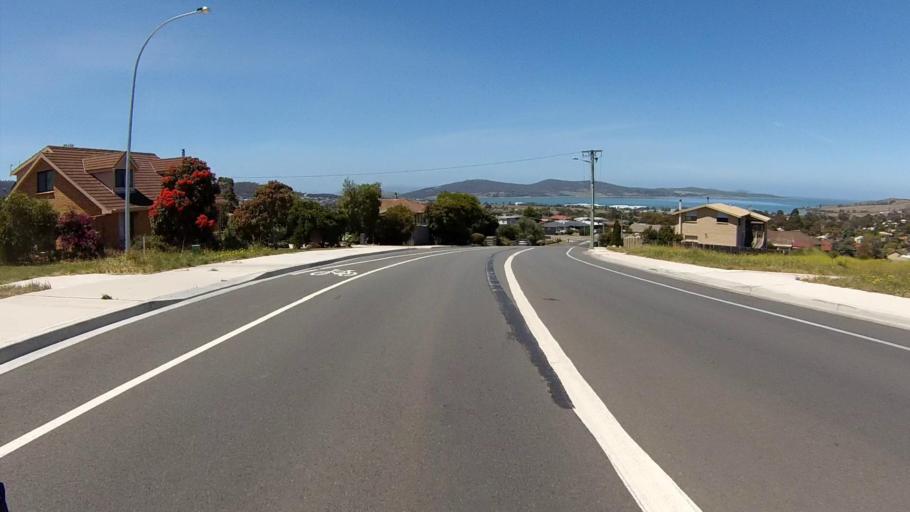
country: AU
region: Tasmania
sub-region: Clarence
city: Rokeby
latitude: -42.8906
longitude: 147.4300
